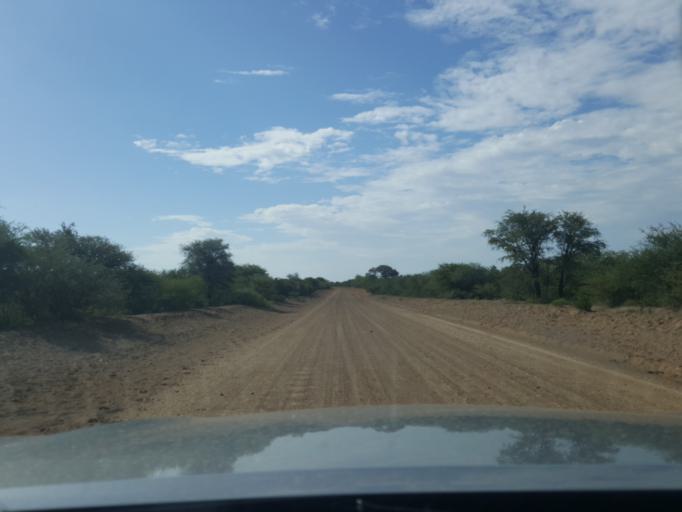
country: BW
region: Kweneng
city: Khudumelapye
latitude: -23.5283
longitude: 24.7228
